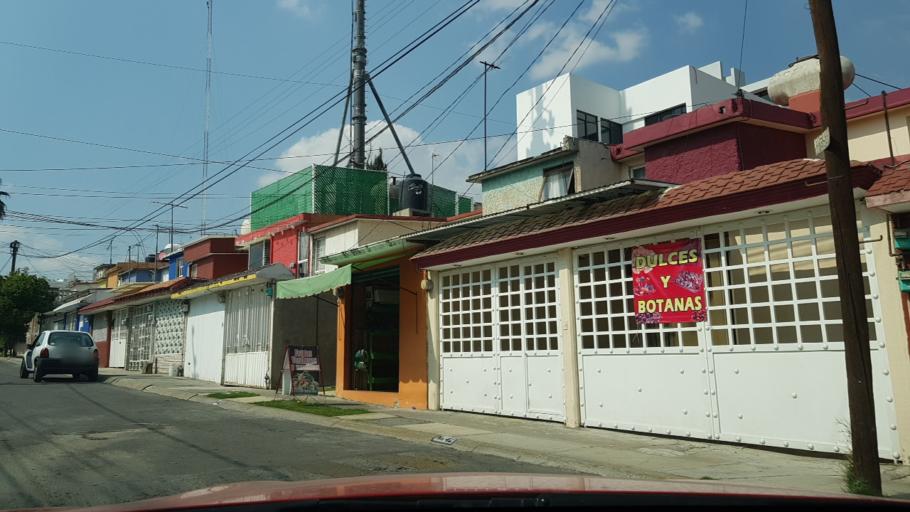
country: MX
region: Mexico
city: Cuautitlan Izcalli
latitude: 19.6473
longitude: -99.2127
